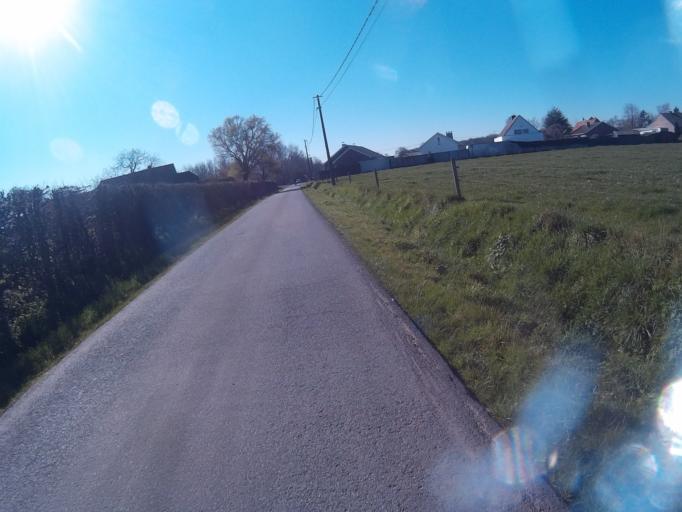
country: BE
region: Flanders
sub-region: Provincie Oost-Vlaanderen
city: Aalter
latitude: 51.1343
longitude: 3.4706
